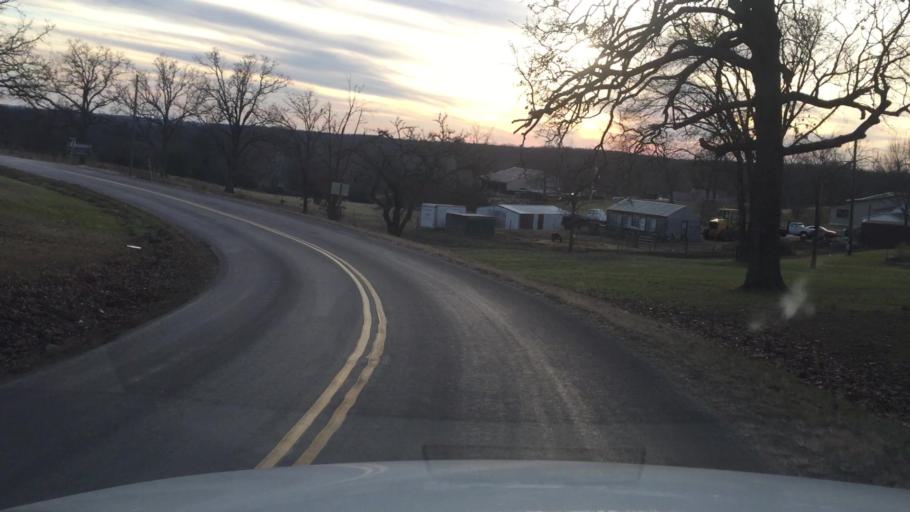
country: US
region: Missouri
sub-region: Miller County
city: Eldon
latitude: 38.3784
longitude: -92.6788
